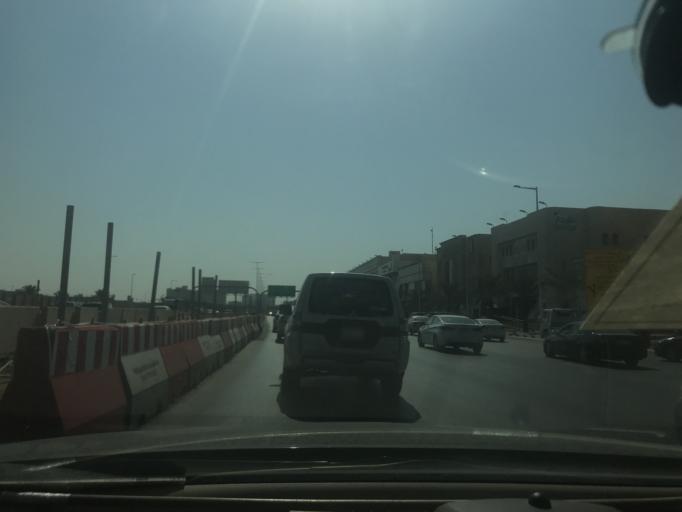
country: SA
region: Ar Riyad
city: Riyadh
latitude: 24.6998
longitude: 46.7229
